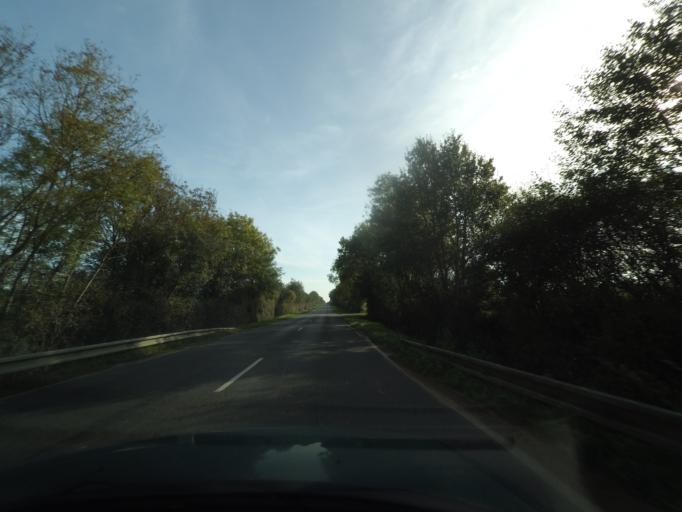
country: FR
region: Pays de la Loire
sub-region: Departement de Maine-et-Loire
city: La Seguiniere
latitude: 47.0584
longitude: -0.9554
